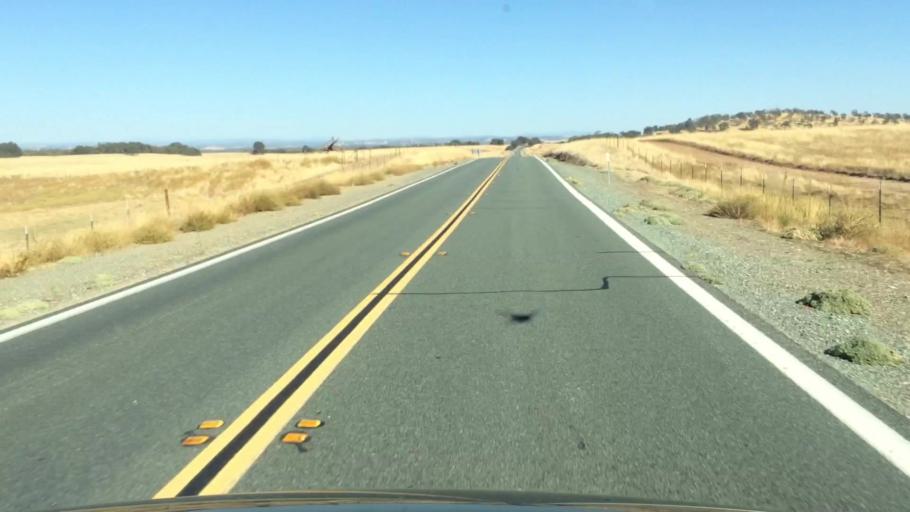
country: US
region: California
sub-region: Amador County
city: Ione
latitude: 38.3866
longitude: -121.0218
